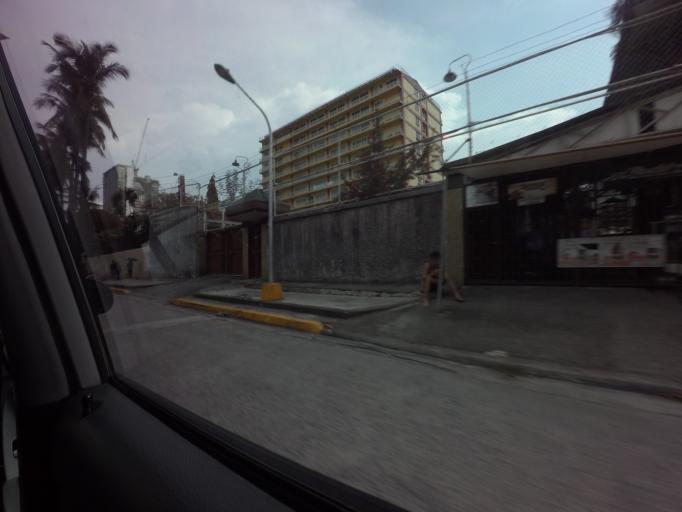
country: PH
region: Metro Manila
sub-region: San Juan
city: San Juan
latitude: 14.6046
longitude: 121.0126
